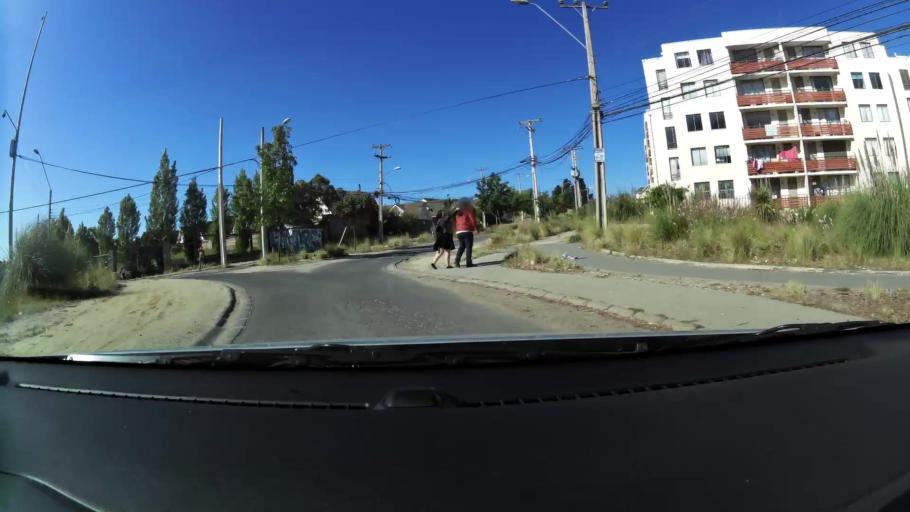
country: CL
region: Valparaiso
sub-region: Provincia de Valparaiso
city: Valparaiso
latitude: -33.1245
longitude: -71.5719
